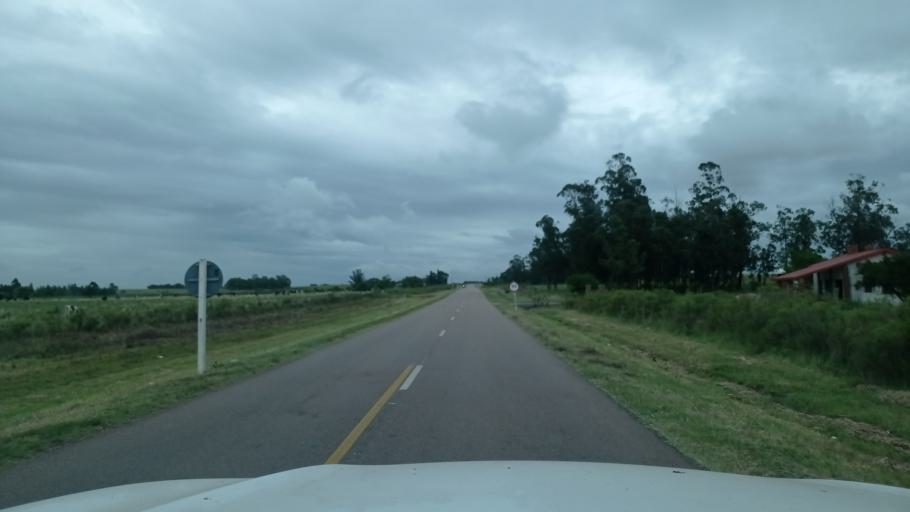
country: UY
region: Canelones
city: Joanico
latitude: -34.5720
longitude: -56.1723
